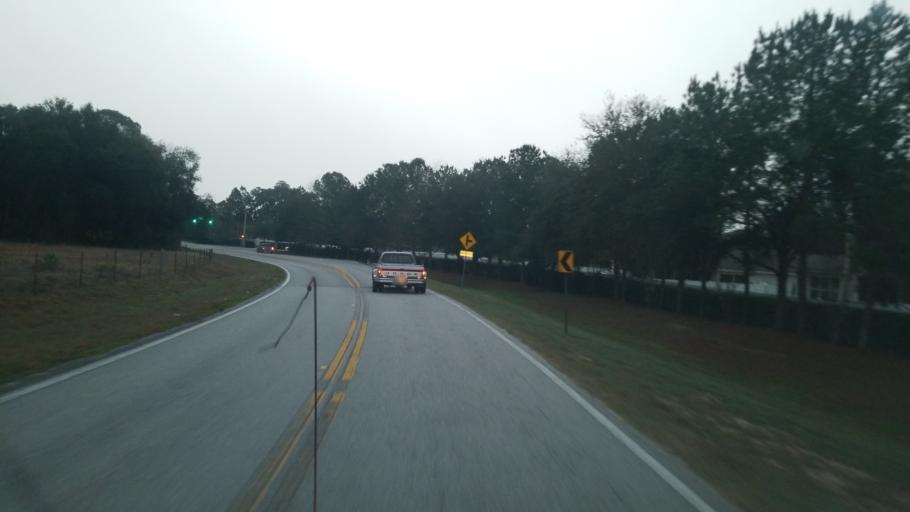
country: US
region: Florida
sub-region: Marion County
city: Ocala
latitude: 29.1484
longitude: -82.2035
